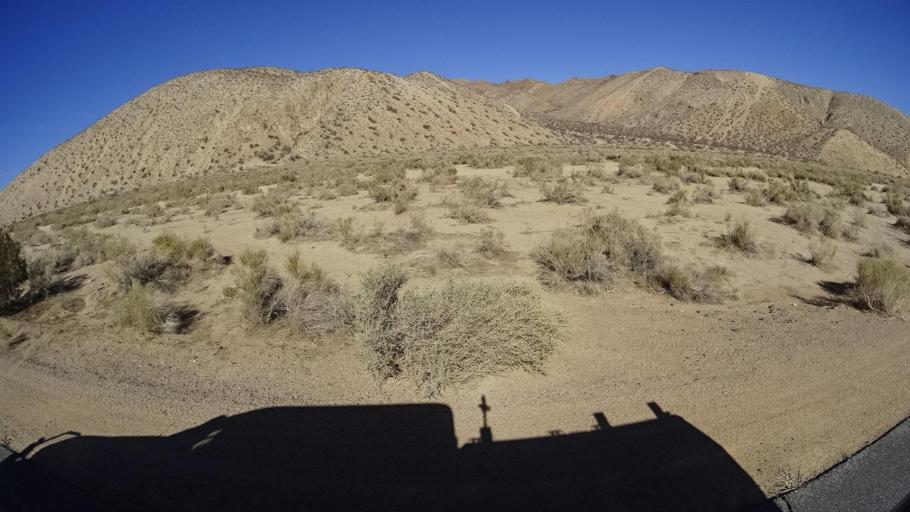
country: US
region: California
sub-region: Kern County
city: California City
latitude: 35.3144
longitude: -118.0643
